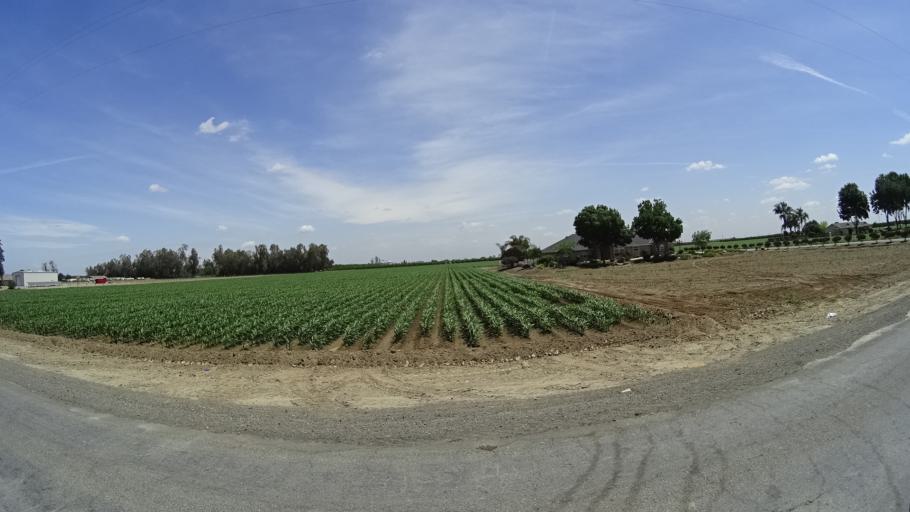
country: US
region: California
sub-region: Kings County
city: Home Garden
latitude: 36.2791
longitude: -119.6728
